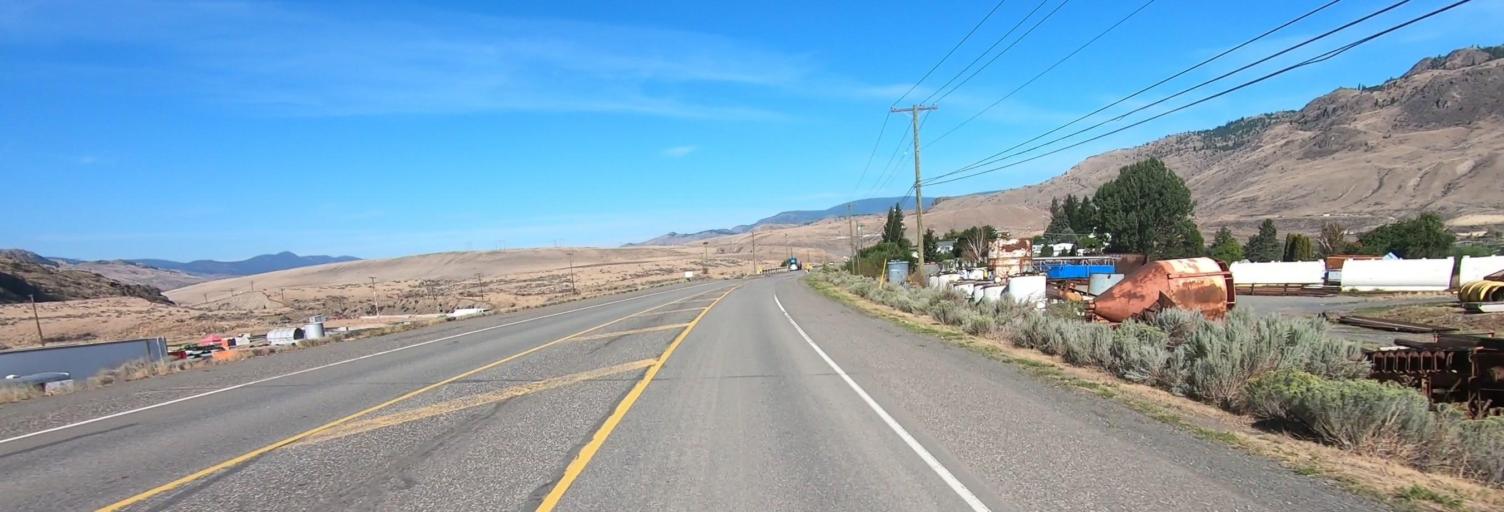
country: CA
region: British Columbia
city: Logan Lake
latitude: 50.7511
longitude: -120.8589
